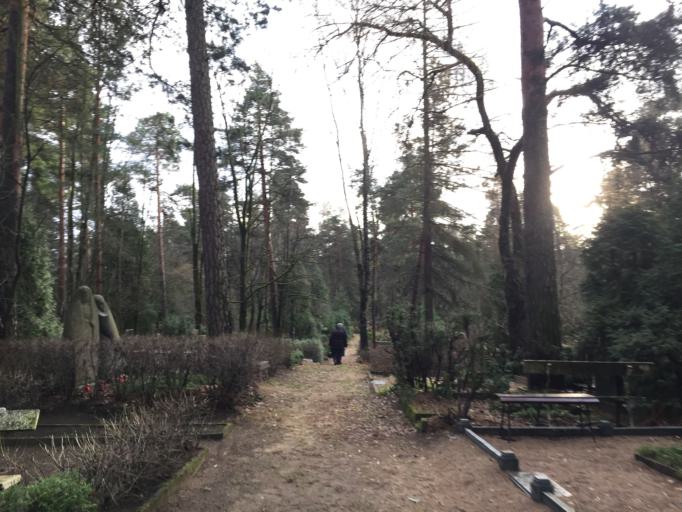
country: LV
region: Riga
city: Jaunciems
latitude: 56.9951
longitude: 24.1387
